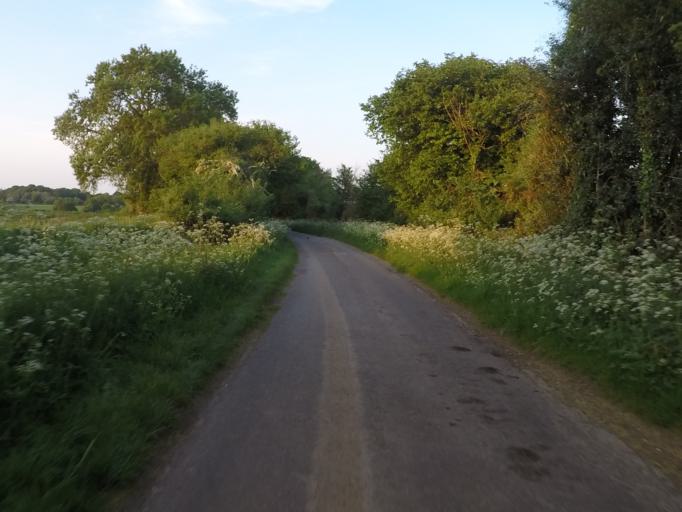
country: GB
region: England
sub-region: Oxfordshire
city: Witney
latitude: 51.8246
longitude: -1.4815
